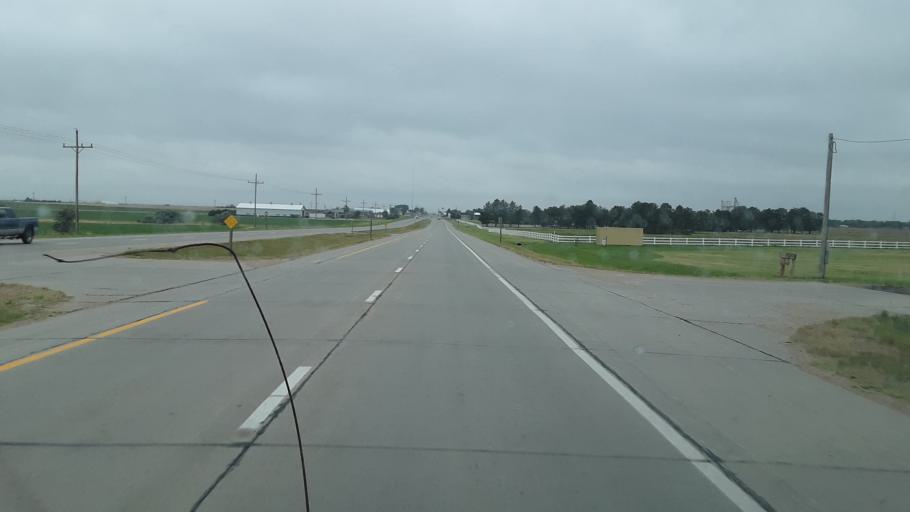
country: US
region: Kansas
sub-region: Logan County
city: Oakley
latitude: 39.1194
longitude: -100.8316
